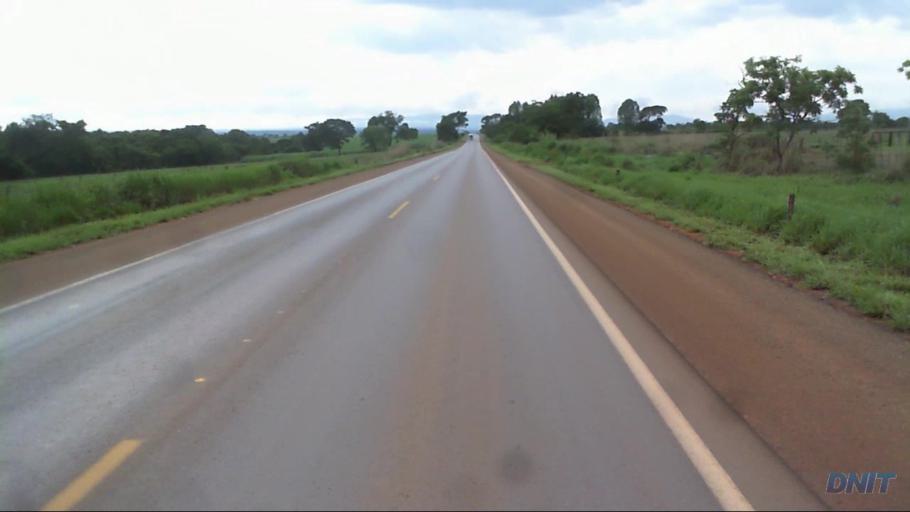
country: BR
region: Goias
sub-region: Uruacu
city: Uruacu
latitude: -14.7083
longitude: -49.1115
